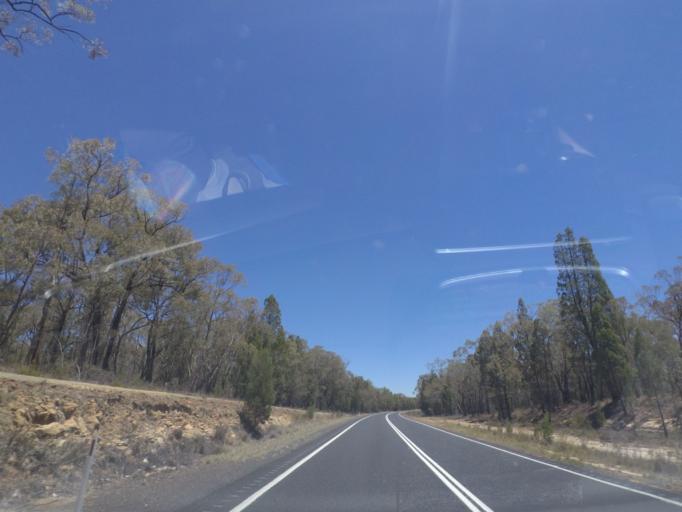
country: AU
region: New South Wales
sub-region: Warrumbungle Shire
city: Coonabarabran
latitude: -31.1938
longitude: 149.3522
